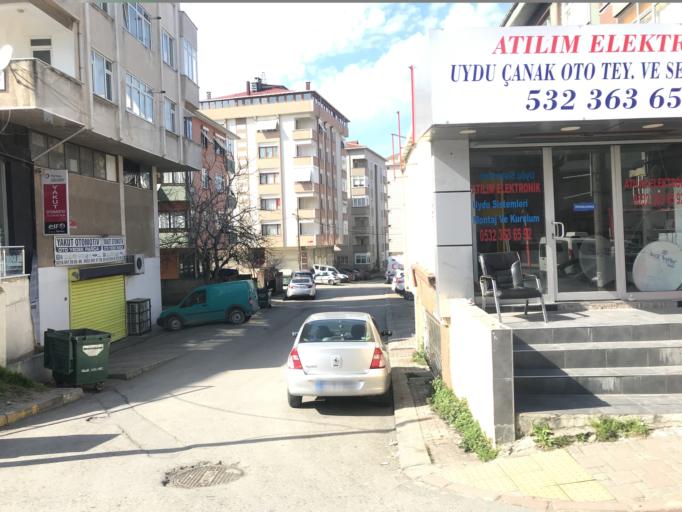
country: TR
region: Istanbul
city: Maltepe
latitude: 40.9320
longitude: 29.1359
